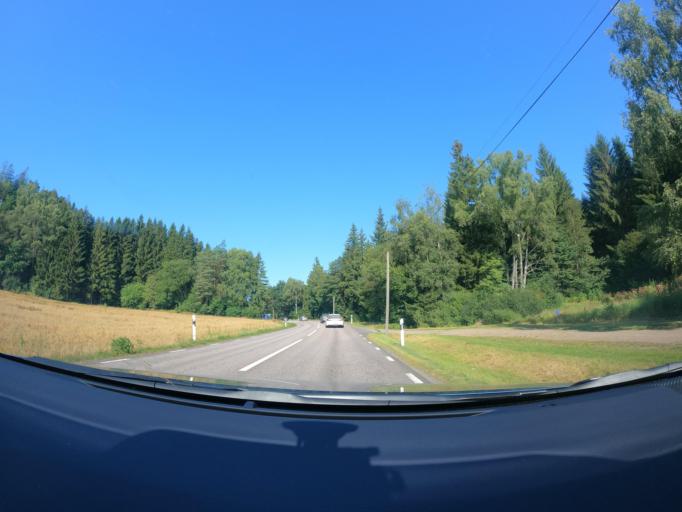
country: SE
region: Halland
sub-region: Falkenbergs Kommun
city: Falkenberg
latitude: 57.0590
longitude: 12.6256
